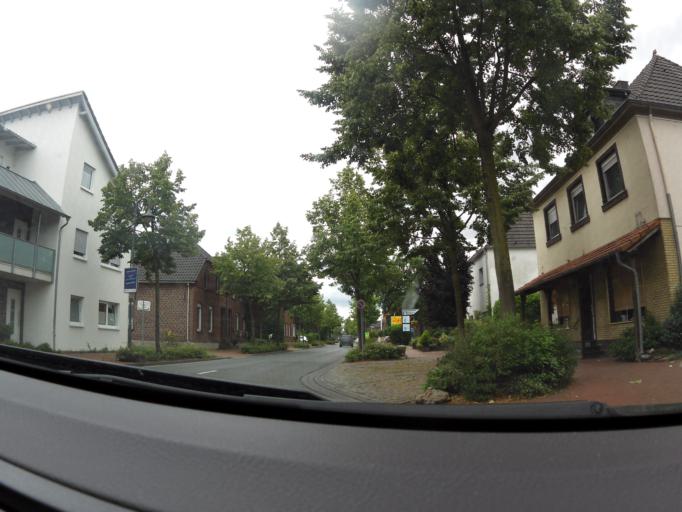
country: DE
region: North Rhine-Westphalia
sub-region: Regierungsbezirk Dusseldorf
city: Sonsbeck
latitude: 51.6065
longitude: 6.3765
